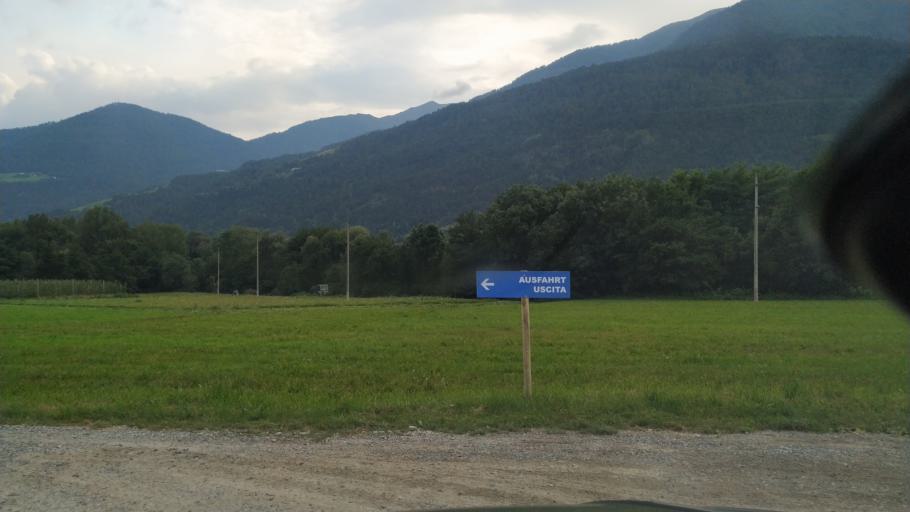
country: IT
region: Trentino-Alto Adige
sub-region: Bolzano
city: Sluderno
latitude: 46.6599
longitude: 10.5703
